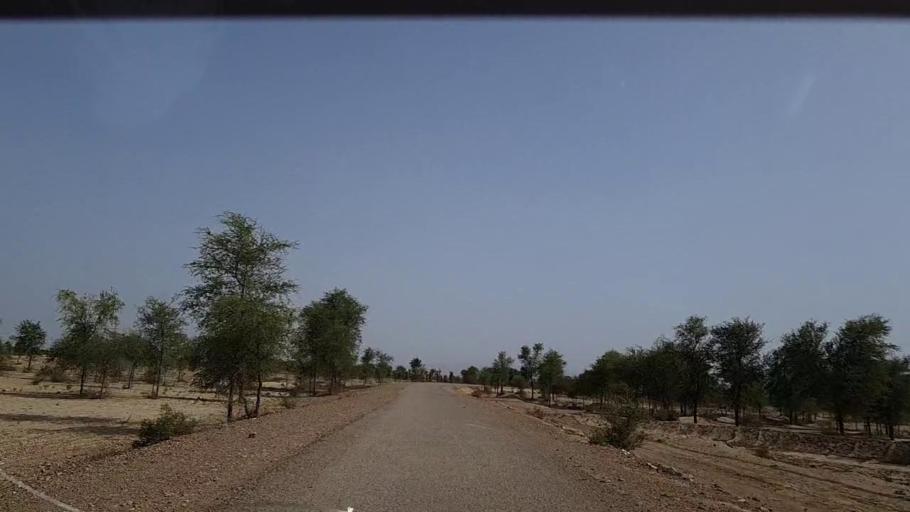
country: PK
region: Sindh
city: Johi
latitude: 26.6107
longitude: 67.4939
